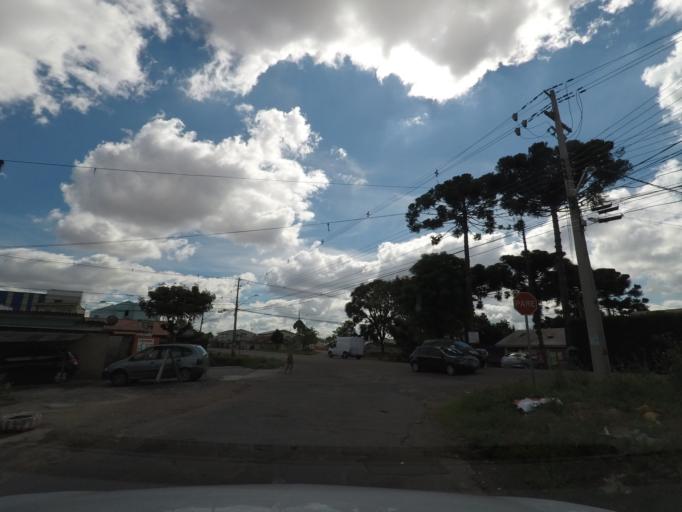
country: BR
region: Parana
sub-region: Sao Jose Dos Pinhais
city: Sao Jose dos Pinhais
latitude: -25.4997
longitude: -49.2275
